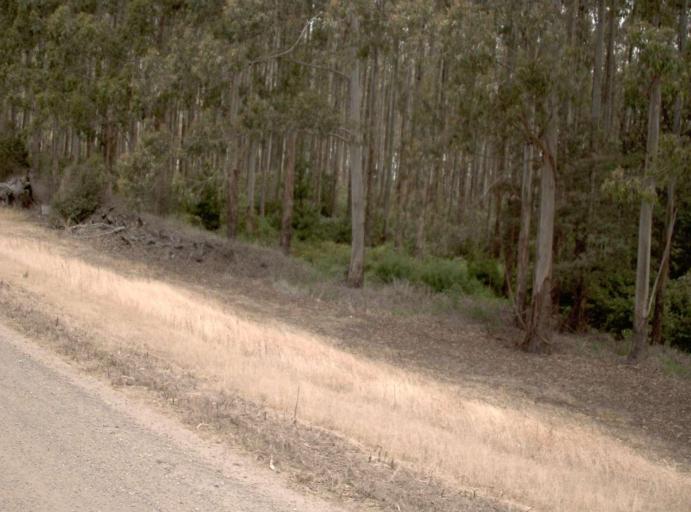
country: AU
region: Victoria
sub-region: Latrobe
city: Traralgon
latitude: -38.3735
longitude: 146.6842
